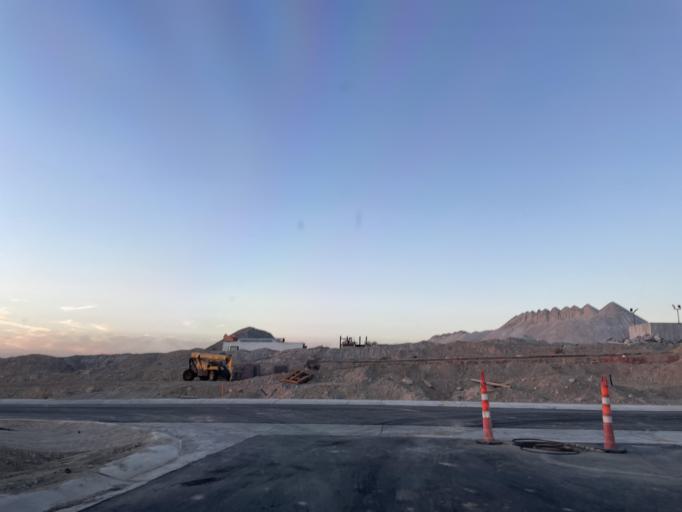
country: US
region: Nevada
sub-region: Clark County
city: Summerlin South
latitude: 36.2558
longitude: -115.3215
